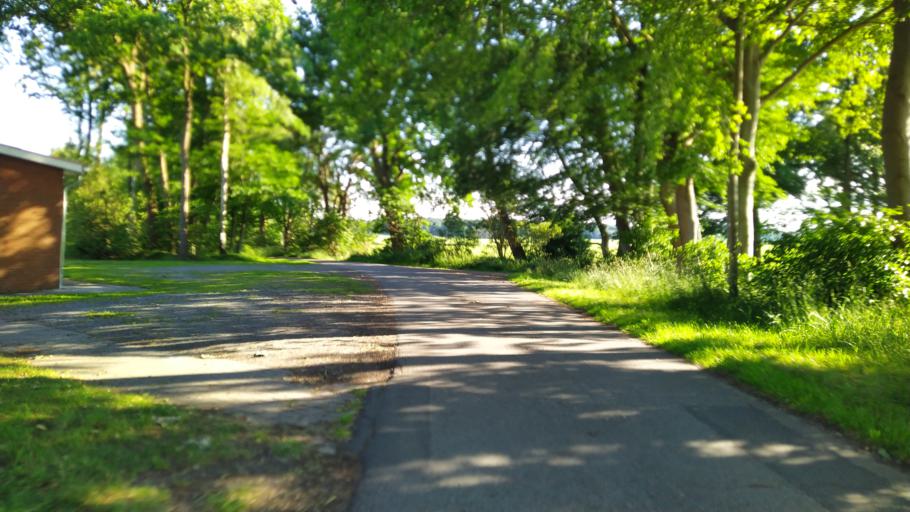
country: DE
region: Lower Saxony
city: Lintig
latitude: 53.5932
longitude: 8.9284
